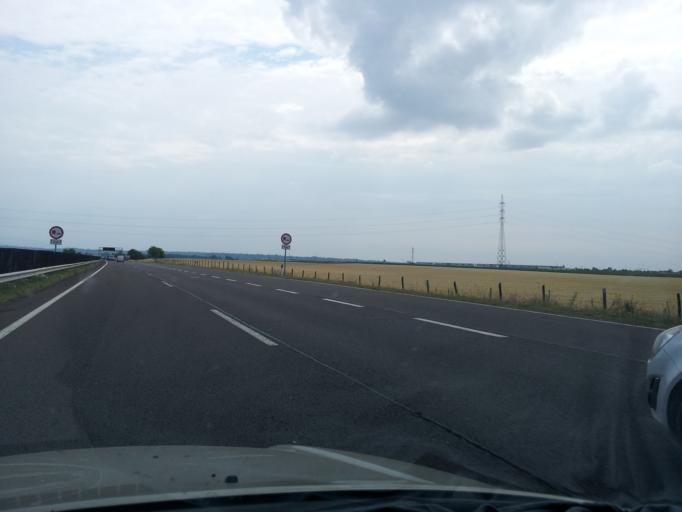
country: HU
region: Heves
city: Hered
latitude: 47.6697
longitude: 19.6295
